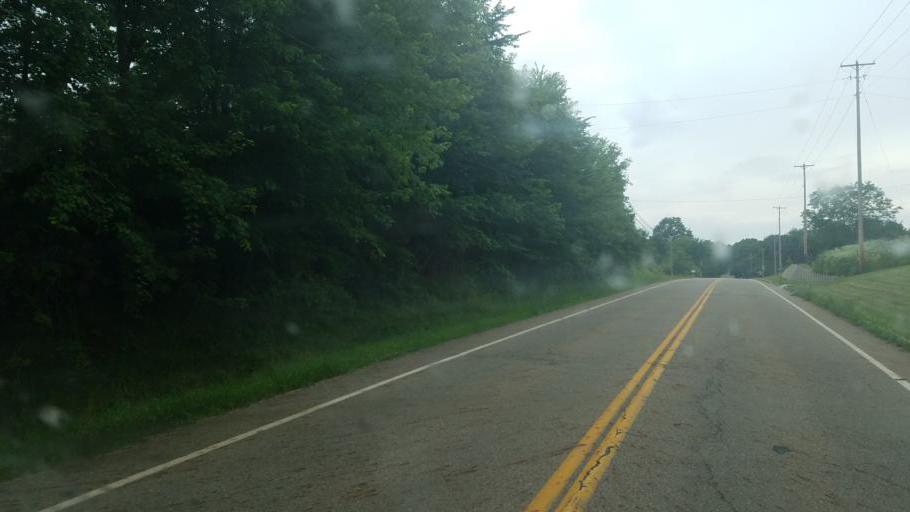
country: US
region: Ohio
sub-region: Summit County
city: Clinton
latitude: 40.9307
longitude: -81.6088
